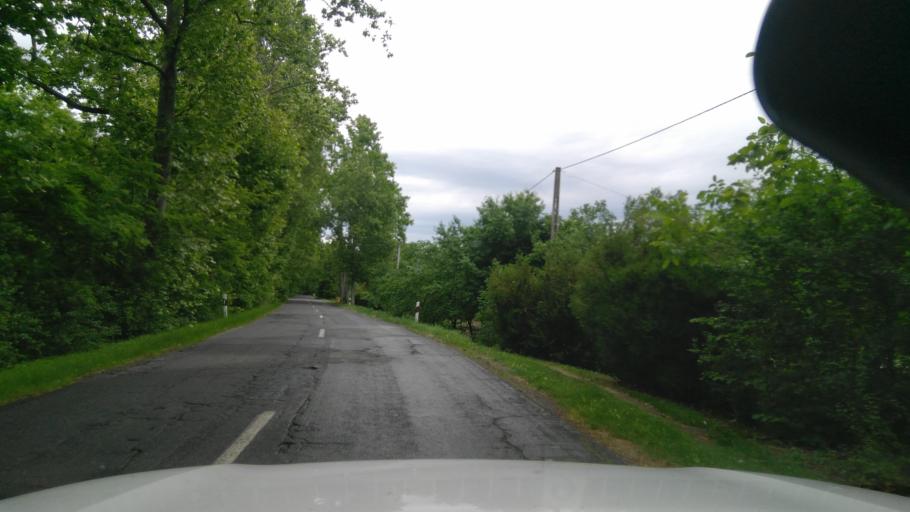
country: HU
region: Bekes
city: Bekescsaba
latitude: 46.7019
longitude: 21.1724
